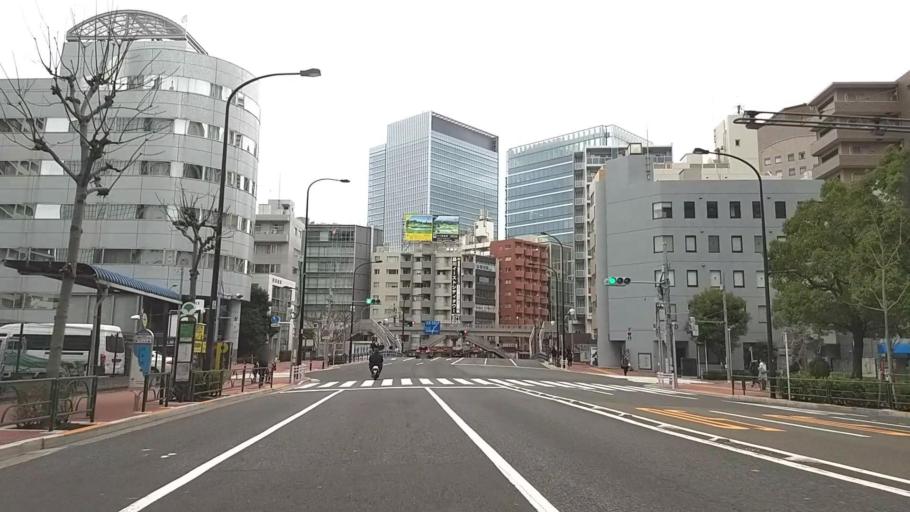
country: JP
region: Tokyo
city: Tokyo
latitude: 35.6408
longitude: 139.7478
